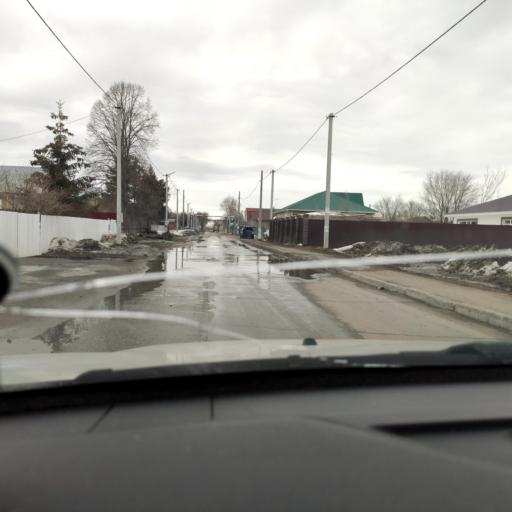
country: RU
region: Samara
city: Kurumoch
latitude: 53.4843
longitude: 50.0336
